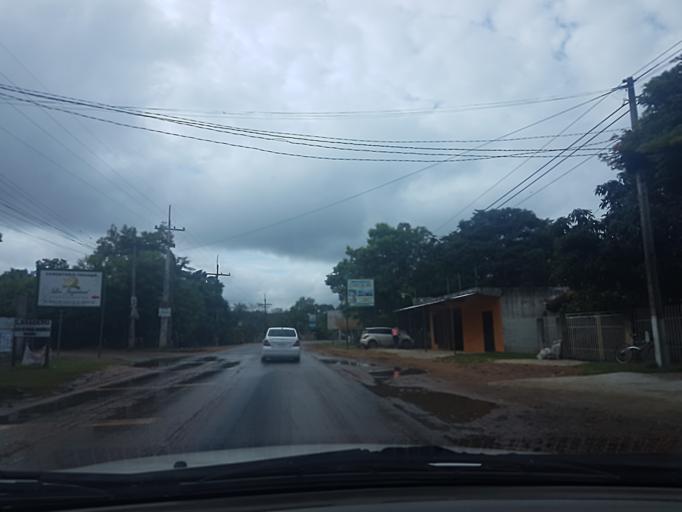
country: PY
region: Central
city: Limpio
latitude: -25.1907
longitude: -57.4638
